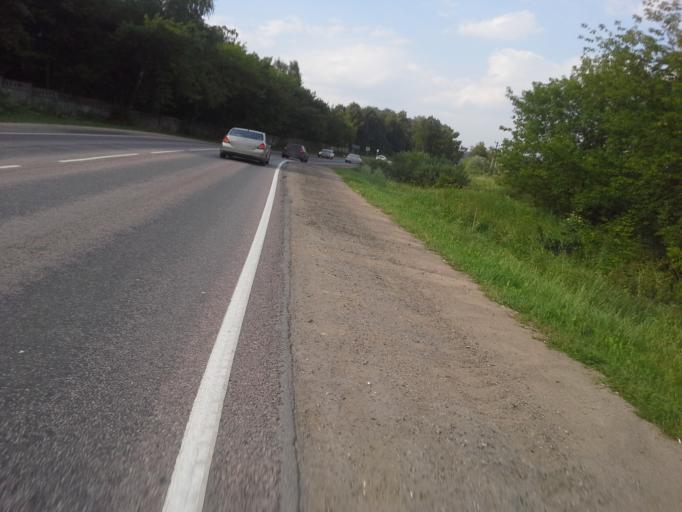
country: RU
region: Moskovskaya
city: Istra
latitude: 55.9024
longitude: 36.8080
